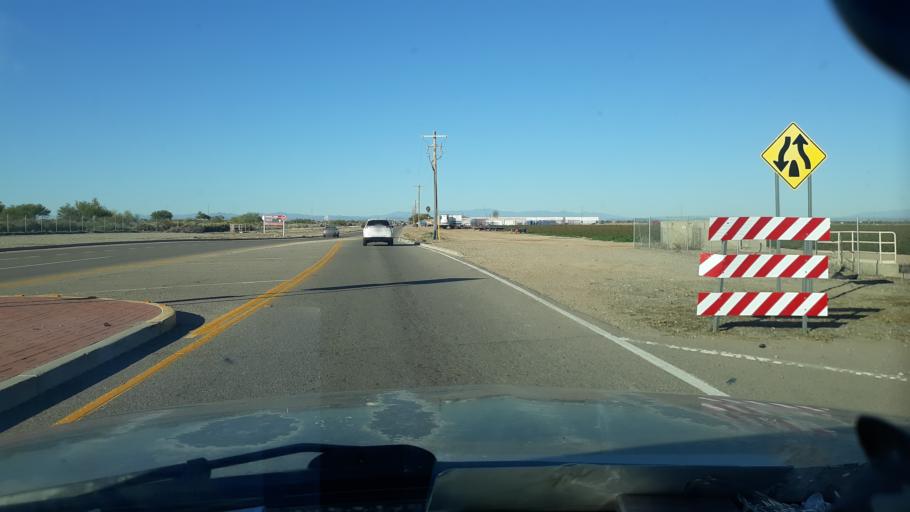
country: US
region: Arizona
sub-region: Maricopa County
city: Citrus Park
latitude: 33.5600
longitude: -112.3935
